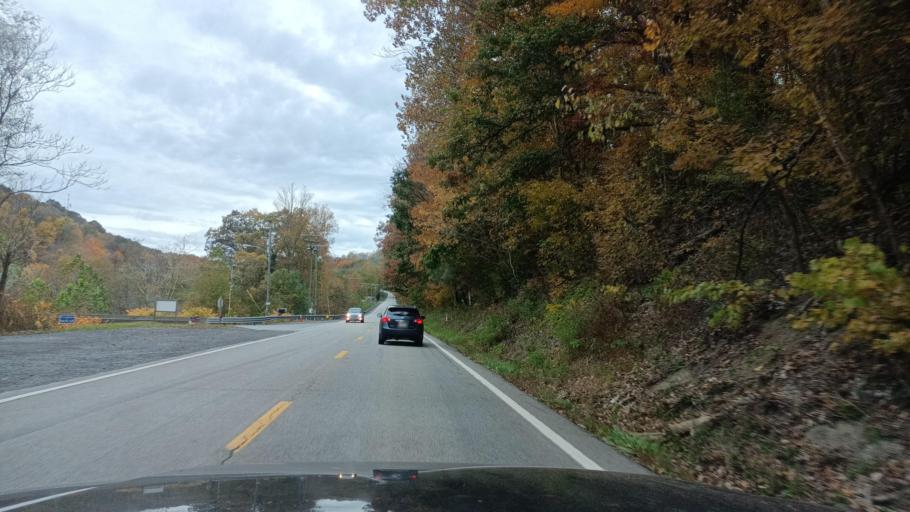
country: US
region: West Virginia
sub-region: Taylor County
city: Grafton
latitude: 39.3418
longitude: -79.9749
